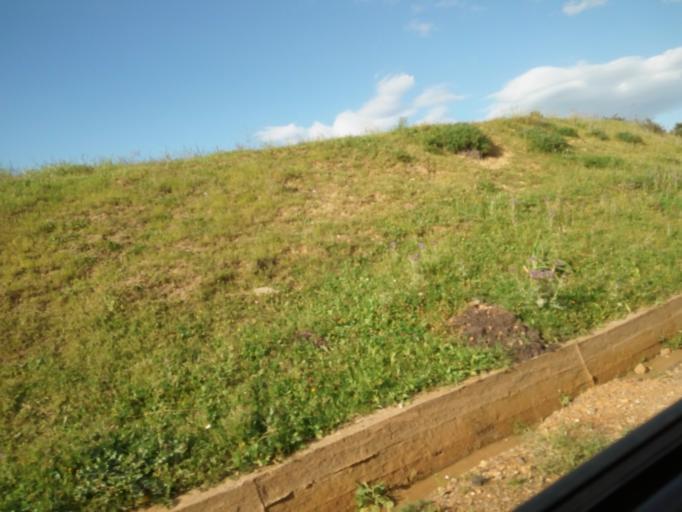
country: DZ
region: Tipaza
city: El Affroun
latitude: 36.3723
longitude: 2.5000
